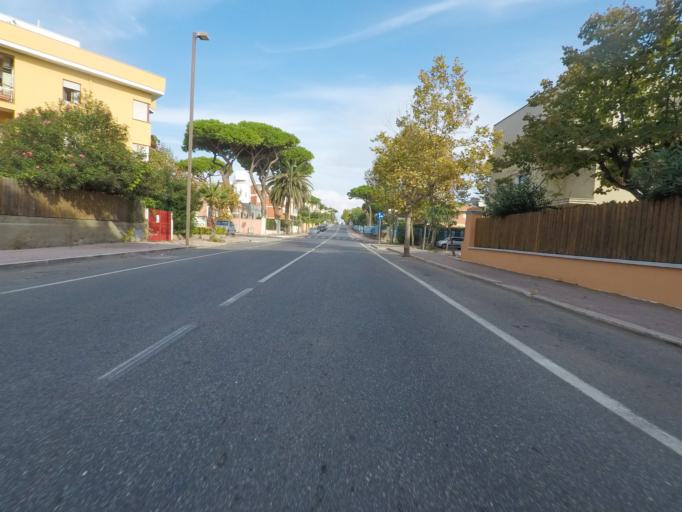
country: IT
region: Latium
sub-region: Citta metropolitana di Roma Capitale
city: Santa Marinella
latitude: 42.0327
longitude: 11.8484
